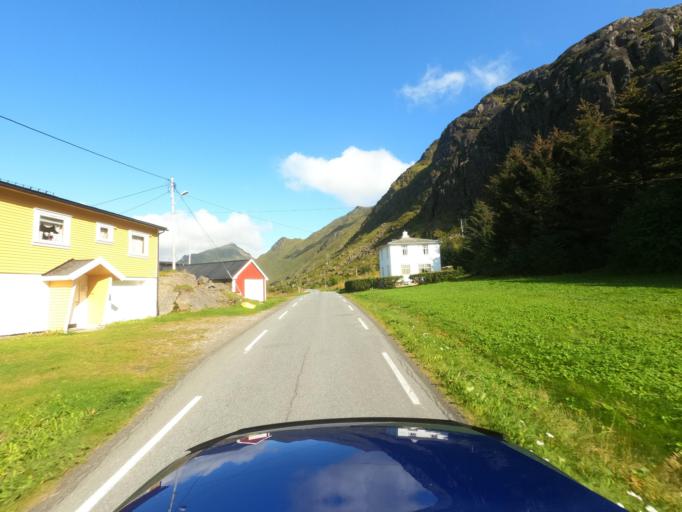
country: NO
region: Nordland
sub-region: Vestvagoy
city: Leknes
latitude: 68.0877
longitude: 13.6412
